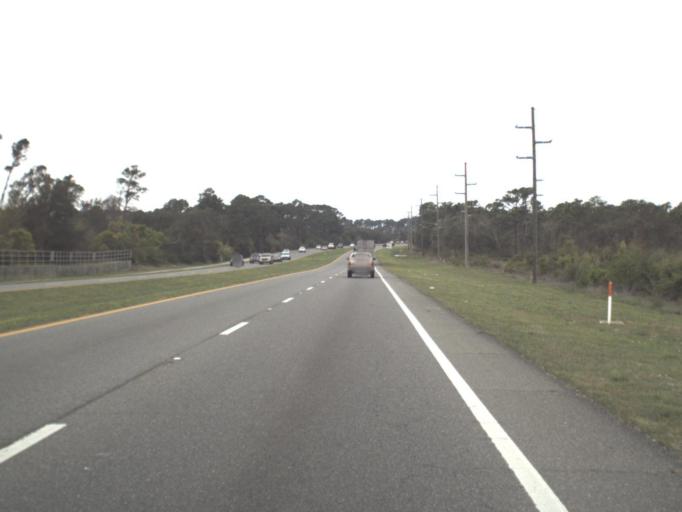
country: US
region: Florida
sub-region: Santa Rosa County
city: Oriole Beach
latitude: 30.3714
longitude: -87.1215
